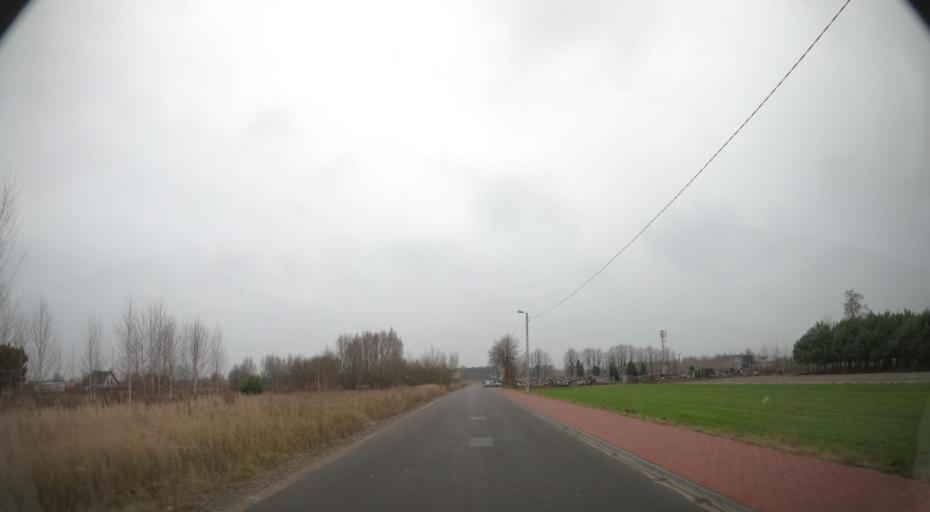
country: PL
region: Masovian Voivodeship
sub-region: Powiat radomski
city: Skaryszew
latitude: 51.3923
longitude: 21.2626
